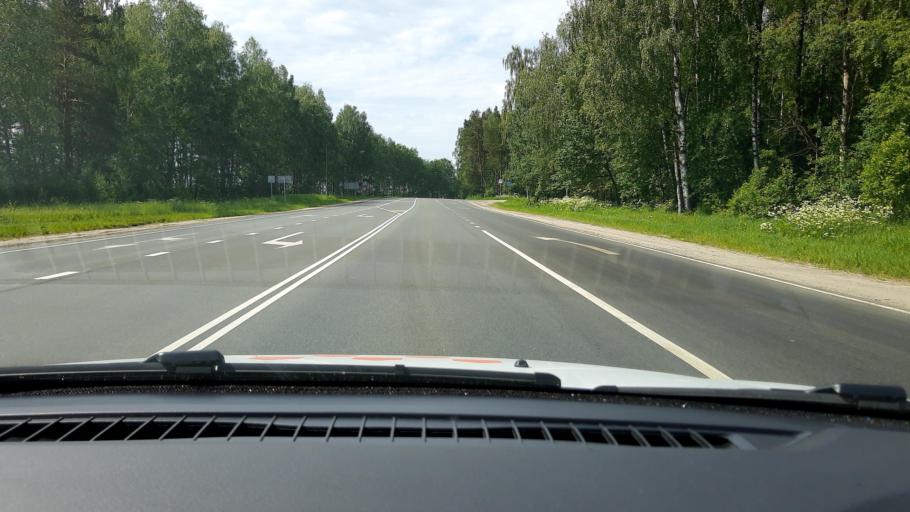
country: RU
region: Nizjnij Novgorod
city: Linda
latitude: 56.6118
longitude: 44.0587
